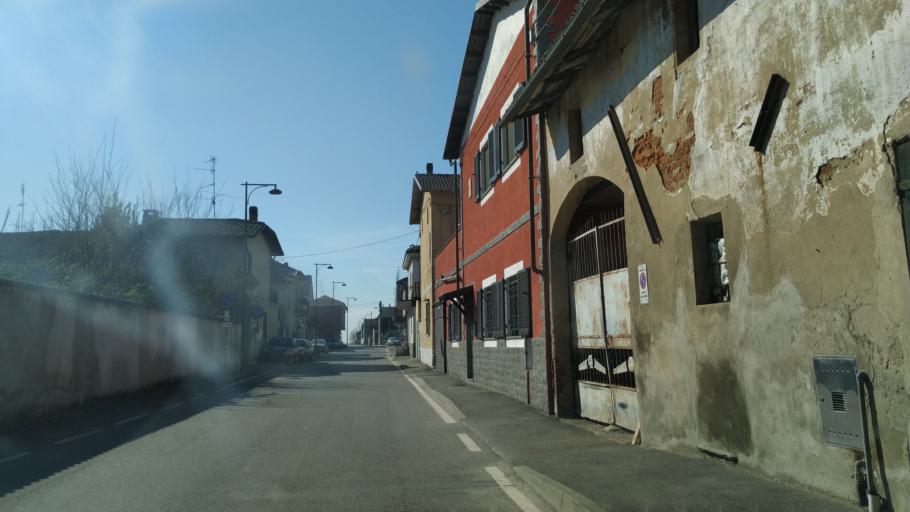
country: IT
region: Piedmont
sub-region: Provincia di Vercelli
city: Asigliano Vercellese
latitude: 45.2580
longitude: 8.4116
